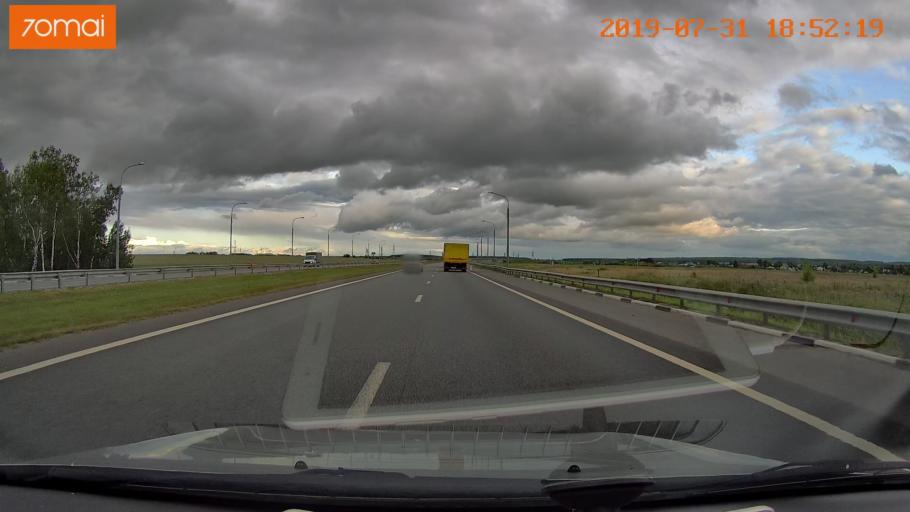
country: RU
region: Moskovskaya
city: Voskresensk
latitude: 55.2149
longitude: 38.6290
